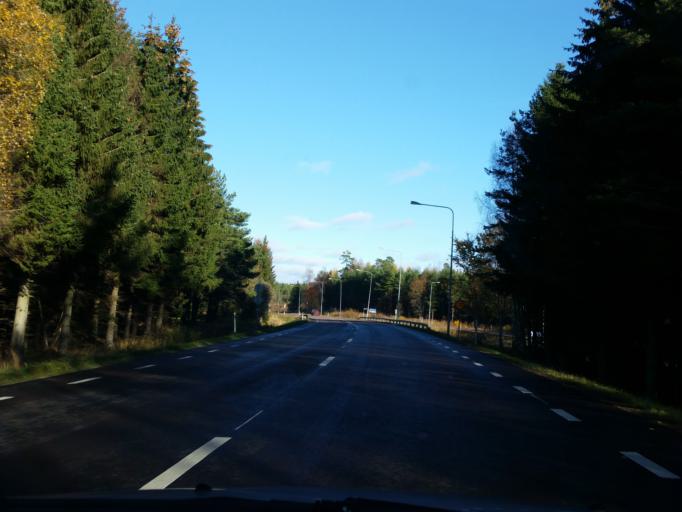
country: AX
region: Alands landsbygd
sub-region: Finstroem
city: Finstroem
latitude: 60.2149
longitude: 19.9774
